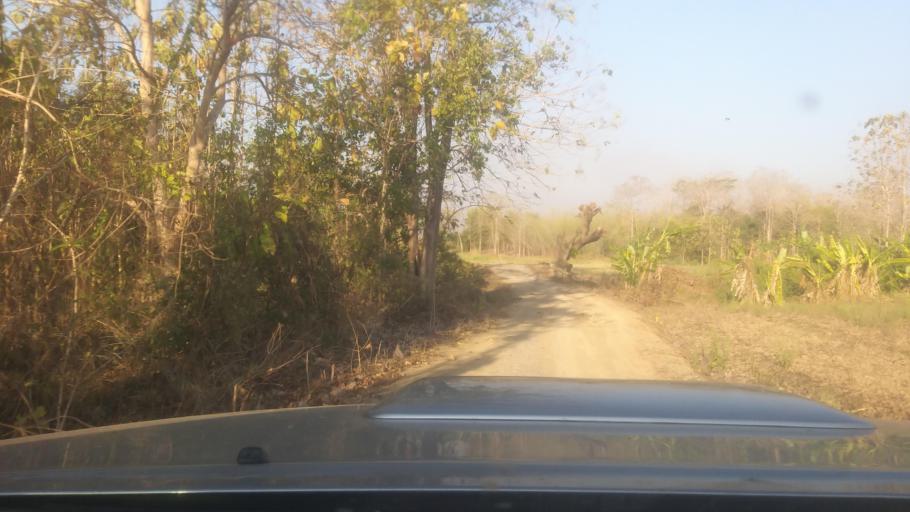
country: TH
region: Phrae
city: Nong Muang Khai
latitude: 18.2731
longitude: 100.0252
